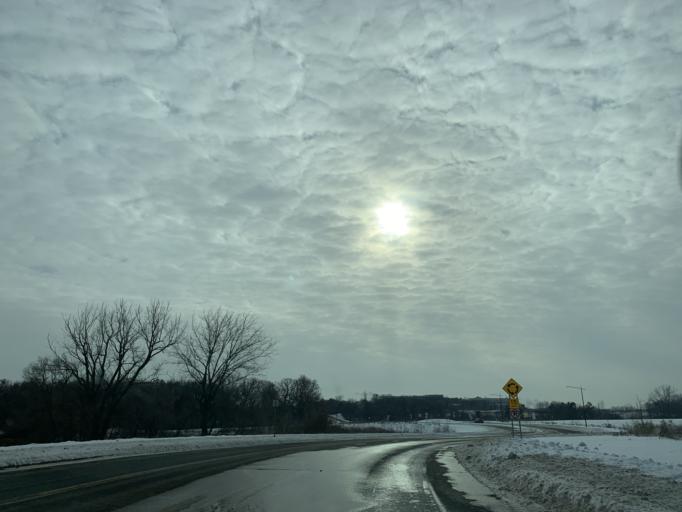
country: US
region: Minnesota
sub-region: Dakota County
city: Mendota Heights
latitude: 44.8587
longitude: -93.1103
